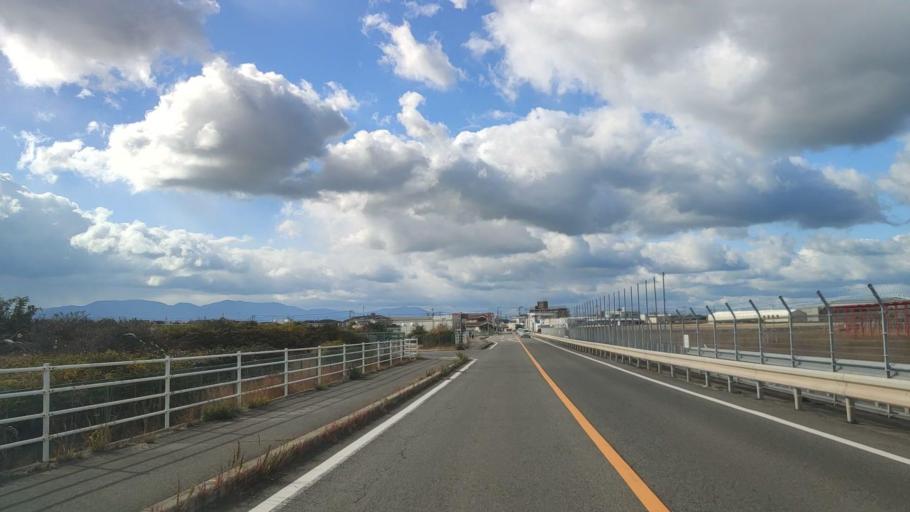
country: JP
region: Ehime
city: Masaki-cho
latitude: 33.8188
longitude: 132.7125
